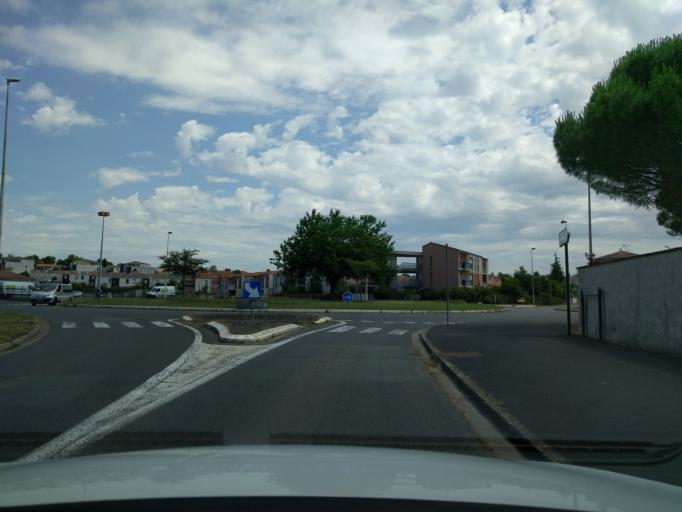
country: FR
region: Poitou-Charentes
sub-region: Departement des Deux-Sevres
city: Niort
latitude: 46.3472
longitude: -0.4828
